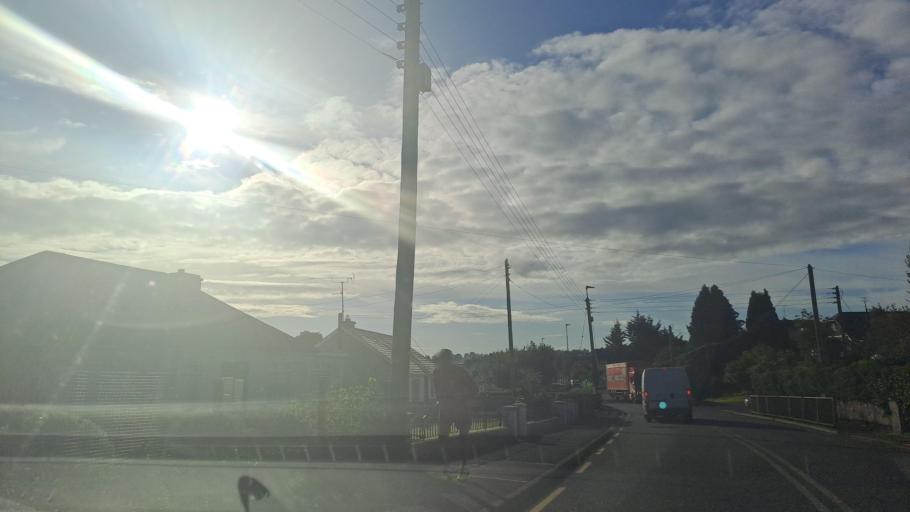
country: IE
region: Ulster
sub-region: County Monaghan
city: Carrickmacross
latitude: 53.9691
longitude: -6.7175
